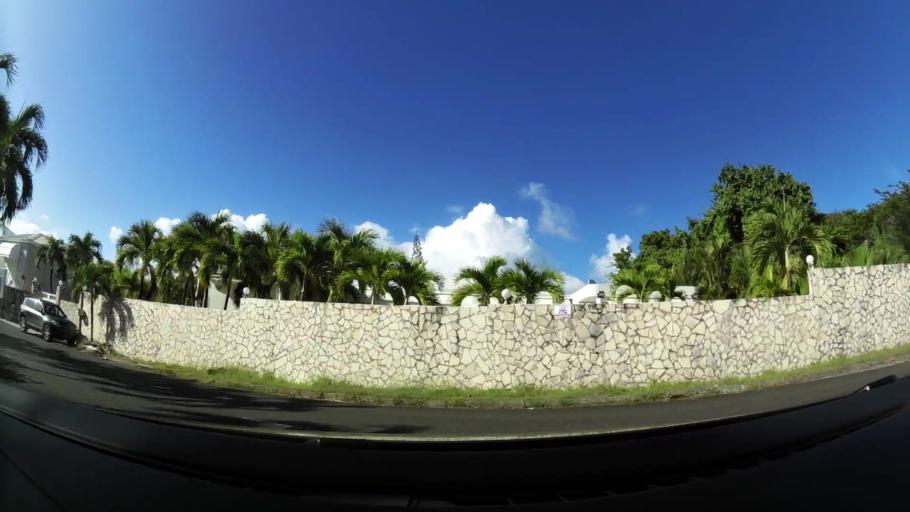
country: GP
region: Guadeloupe
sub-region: Guadeloupe
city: Le Gosier
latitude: 16.2030
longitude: -61.4701
